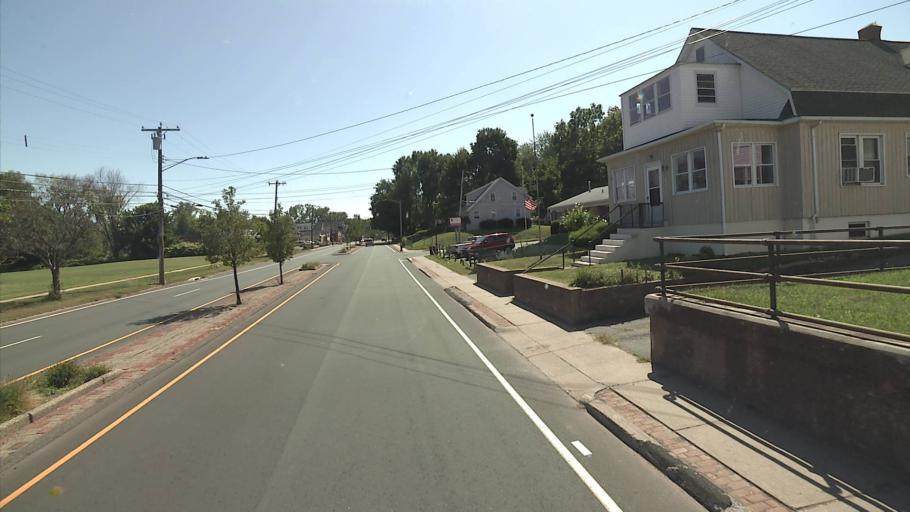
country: US
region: Connecticut
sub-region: Hartford County
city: South Windsor
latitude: 41.8158
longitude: -72.6571
